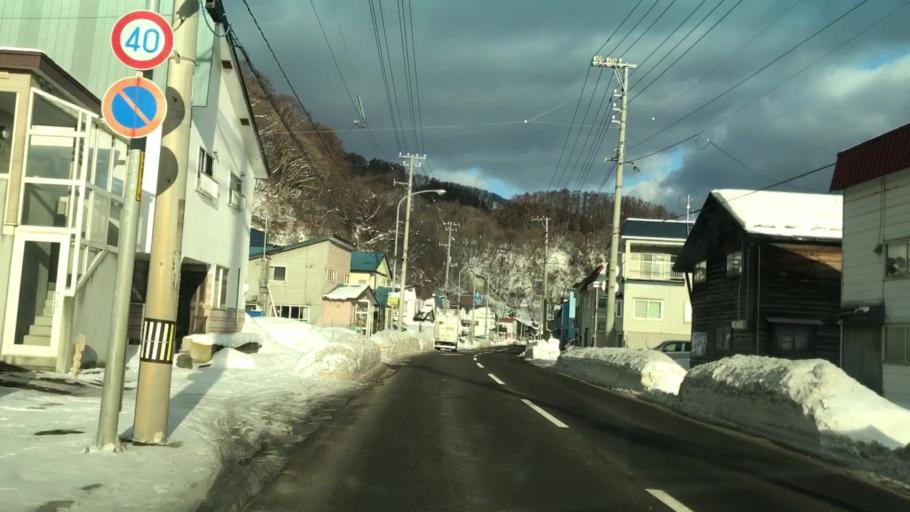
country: JP
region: Hokkaido
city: Yoichi
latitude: 43.2718
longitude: 140.6364
